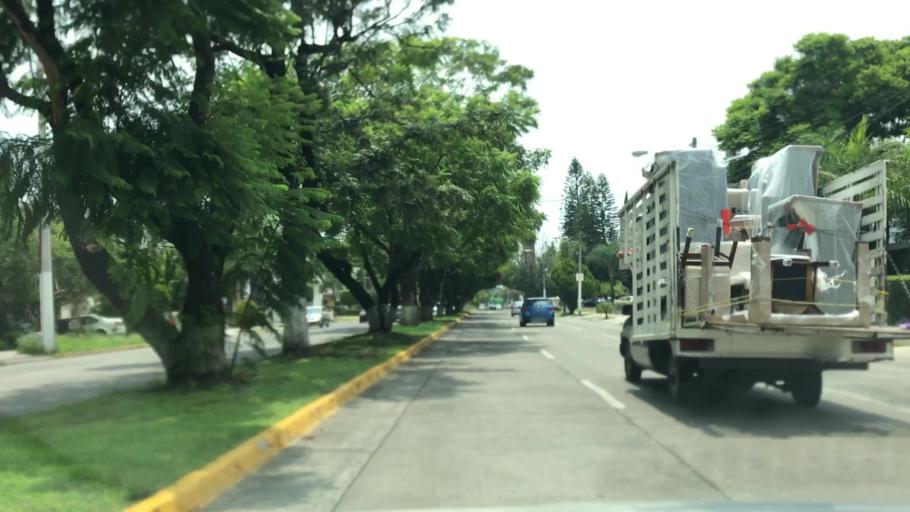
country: MX
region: Jalisco
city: Guadalajara
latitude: 20.6505
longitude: -103.4165
